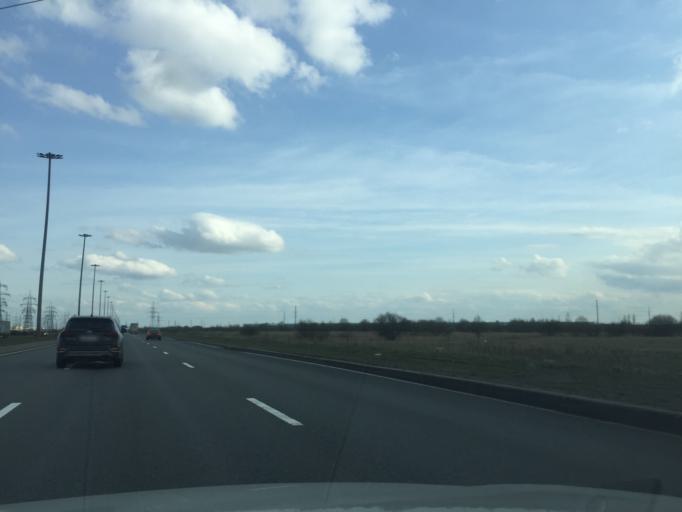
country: RU
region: St.-Petersburg
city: Petro-Slavyanka
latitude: 59.7582
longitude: 30.5154
